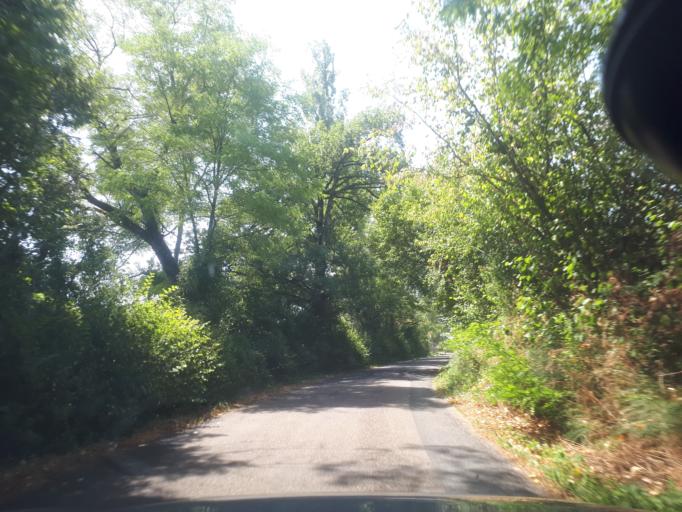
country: FR
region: Midi-Pyrenees
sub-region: Departement du Lot
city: Gourdon
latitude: 44.7550
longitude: 1.3444
